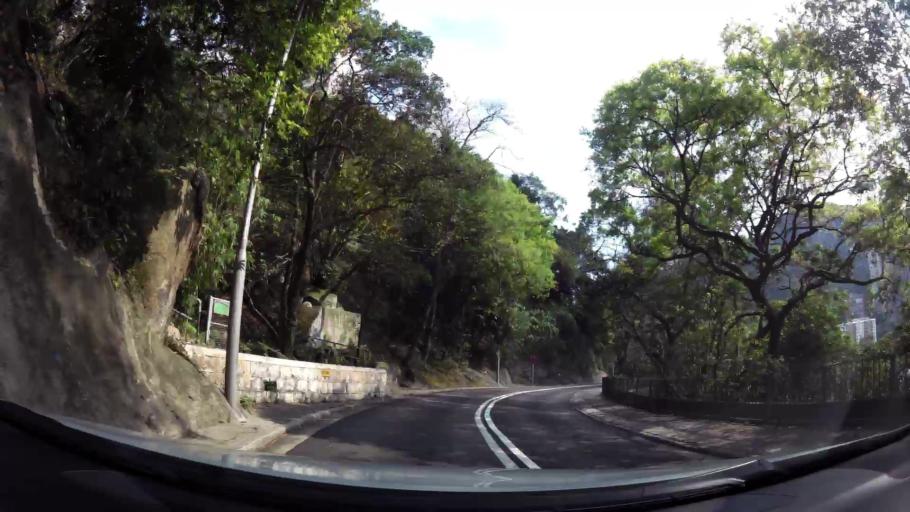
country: HK
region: Wanchai
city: Wan Chai
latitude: 22.2671
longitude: 114.1906
